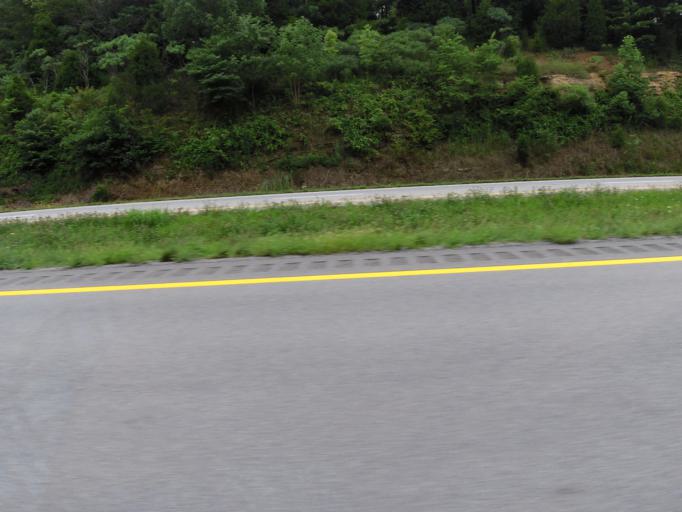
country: US
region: Kentucky
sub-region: Ohio County
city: Oak Grove
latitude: 37.4110
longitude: -86.5302
